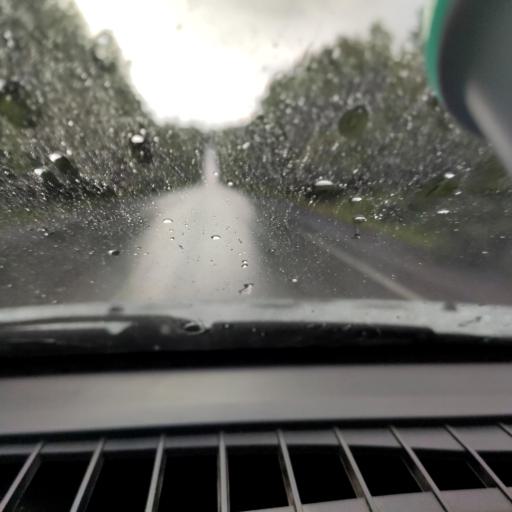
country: RU
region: Chelyabinsk
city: Syrostan
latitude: 55.1188
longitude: 59.8349
